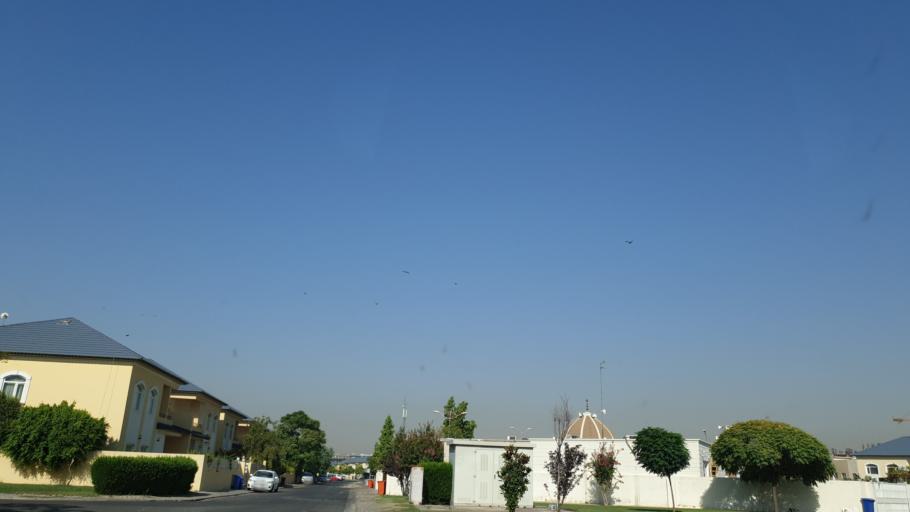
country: IQ
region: Arbil
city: Erbil
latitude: 36.1882
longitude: 43.9708
